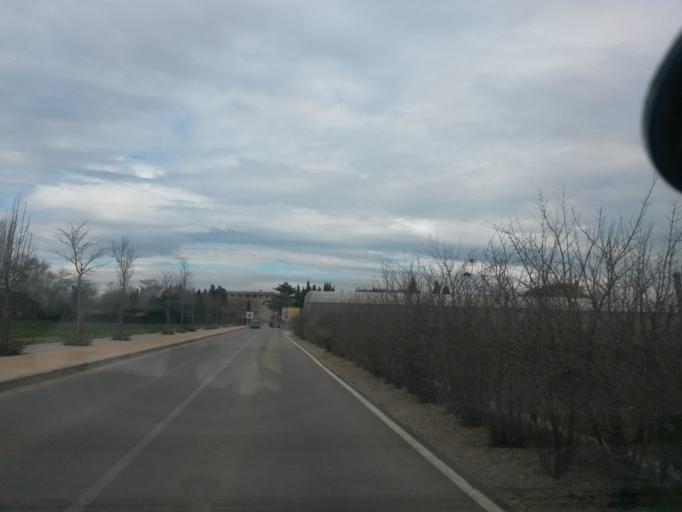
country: ES
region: Catalonia
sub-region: Provincia de Girona
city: Vilabertran
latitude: 42.2799
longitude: 2.9821
